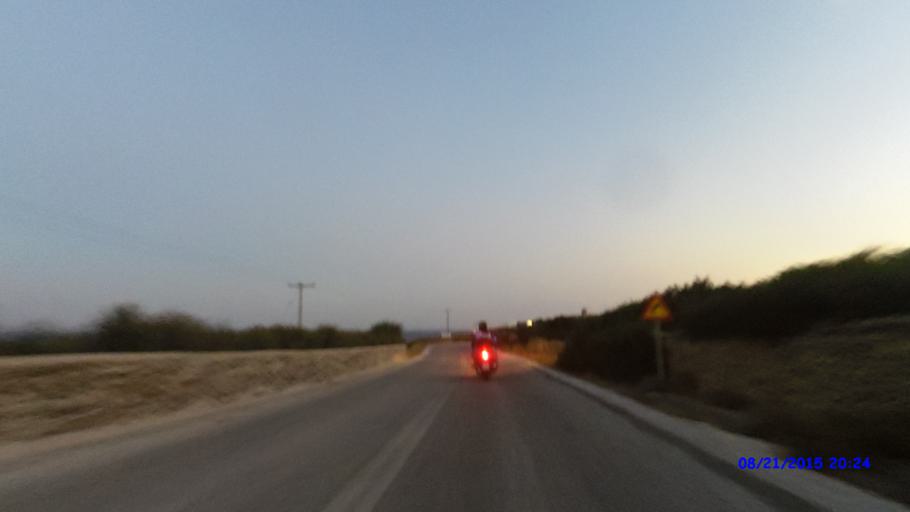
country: GR
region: South Aegean
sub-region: Nomos Kykladon
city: Antiparos
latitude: 36.9883
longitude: 25.0722
